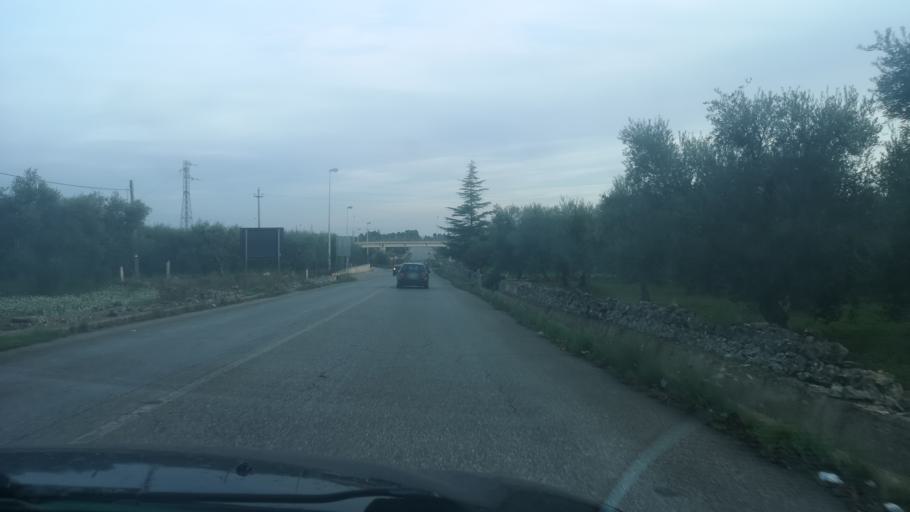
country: IT
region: Apulia
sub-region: Provincia di Bari
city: Cassano delle Murge
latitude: 40.8979
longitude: 16.7734
